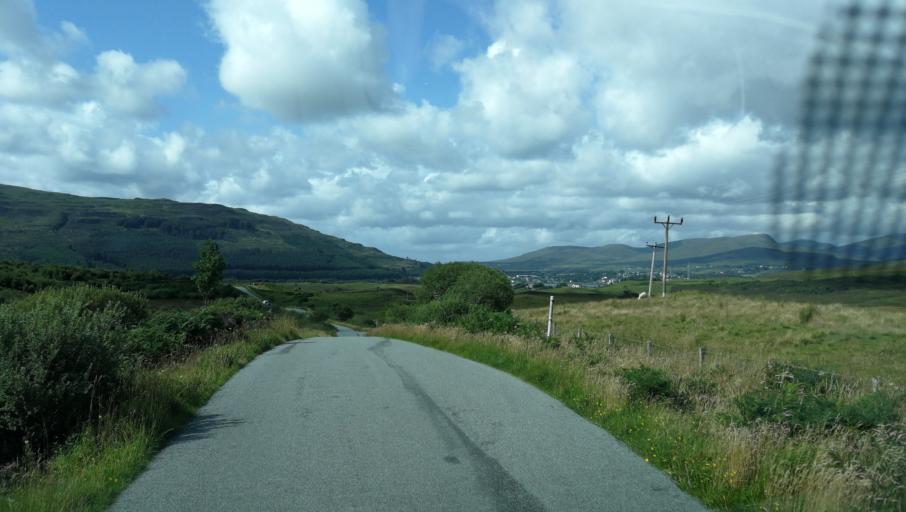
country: GB
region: Scotland
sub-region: Highland
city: Portree
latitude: 57.3810
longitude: -6.1724
